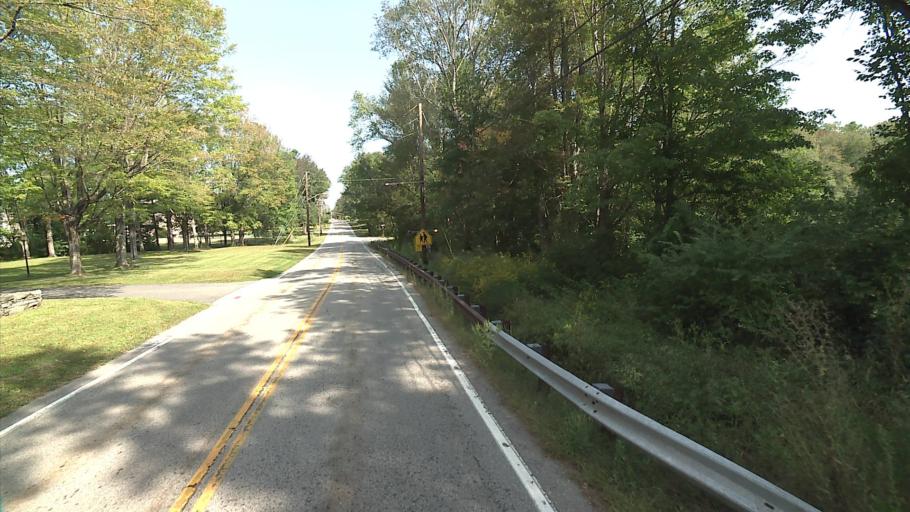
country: US
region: Connecticut
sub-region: Windham County
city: South Woodstock
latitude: 41.9251
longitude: -71.9566
